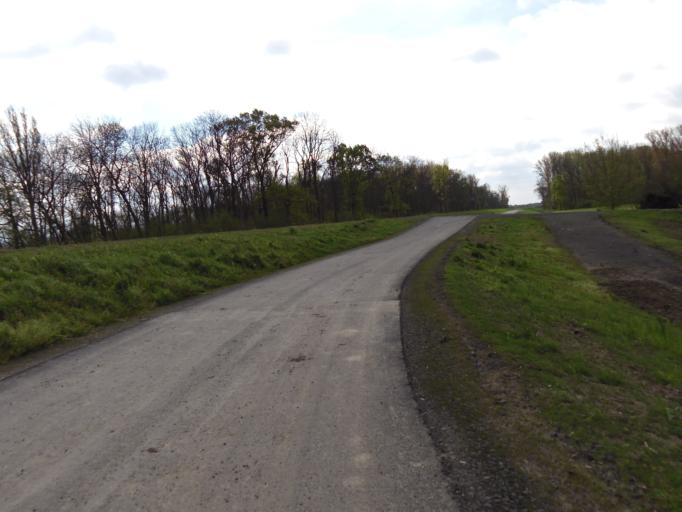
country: DE
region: Rheinland-Pfalz
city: Eich
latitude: 49.6980
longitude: 8.3899
